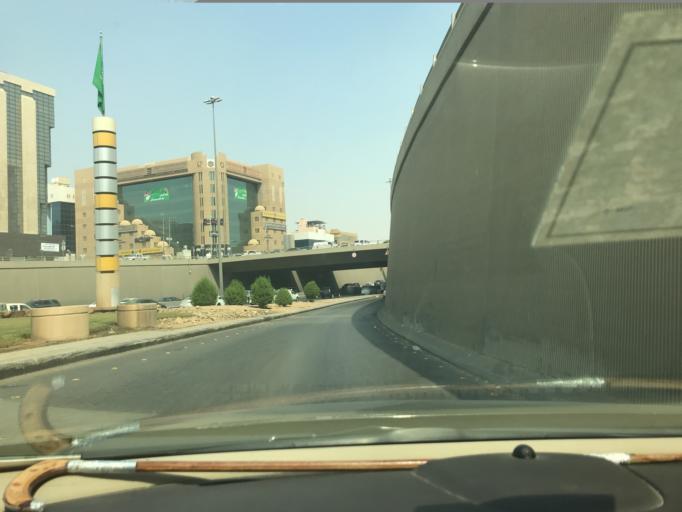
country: SA
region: Ar Riyad
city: Riyadh
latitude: 24.6796
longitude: 46.6915
